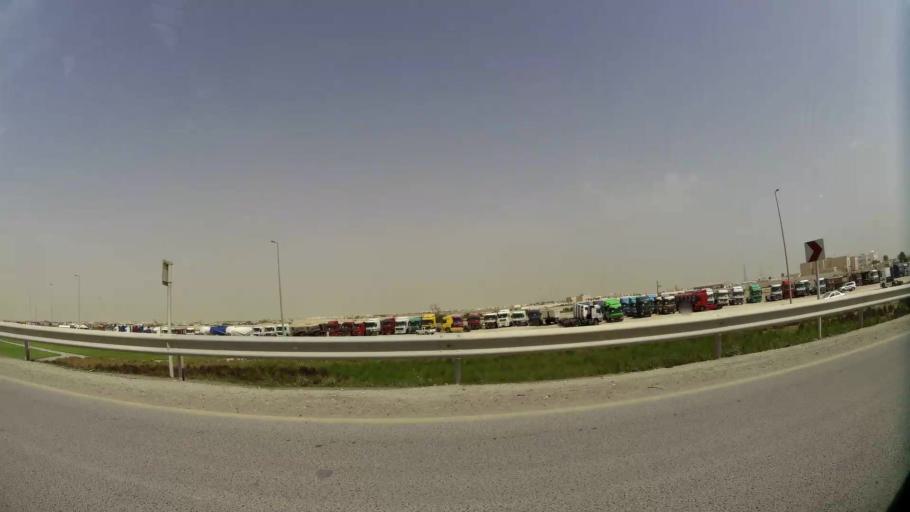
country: QA
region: Baladiyat ar Rayyan
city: Ar Rayyan
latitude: 25.2131
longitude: 51.4068
